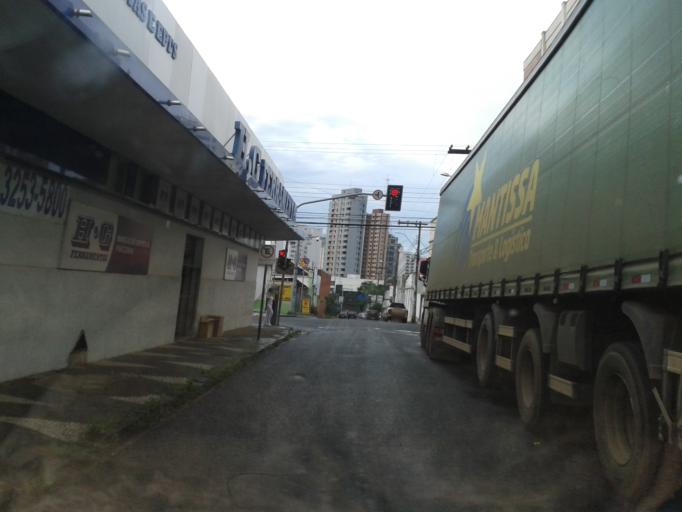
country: BR
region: Minas Gerais
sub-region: Uberlandia
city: Uberlandia
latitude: -18.9127
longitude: -48.2802
